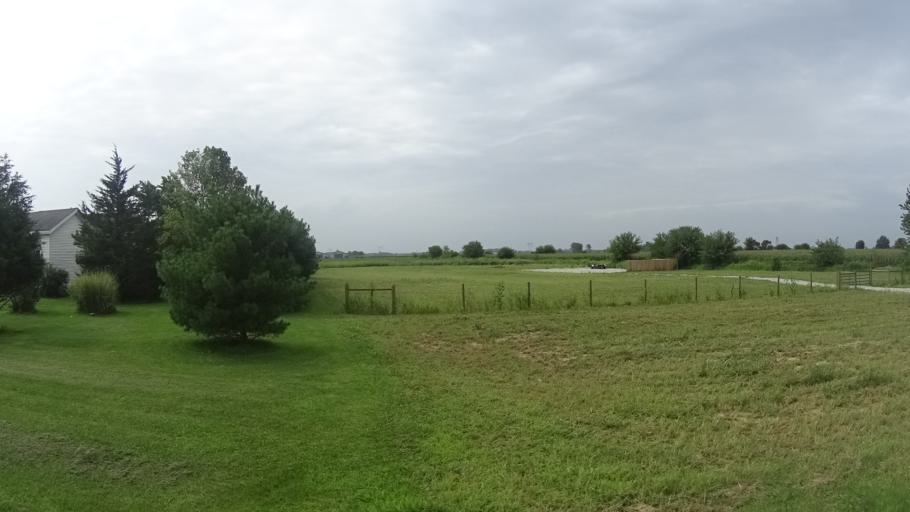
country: US
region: Indiana
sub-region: Madison County
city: Ingalls
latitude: 40.0125
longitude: -85.8084
